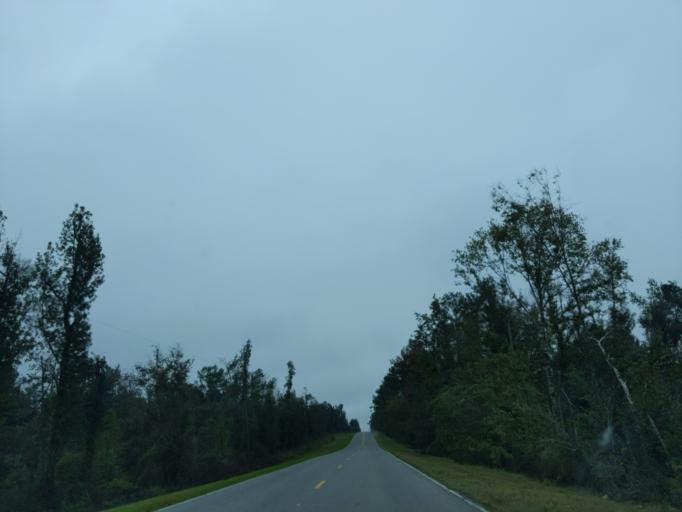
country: US
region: Florida
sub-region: Jackson County
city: Sneads
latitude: 30.6530
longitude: -84.9371
